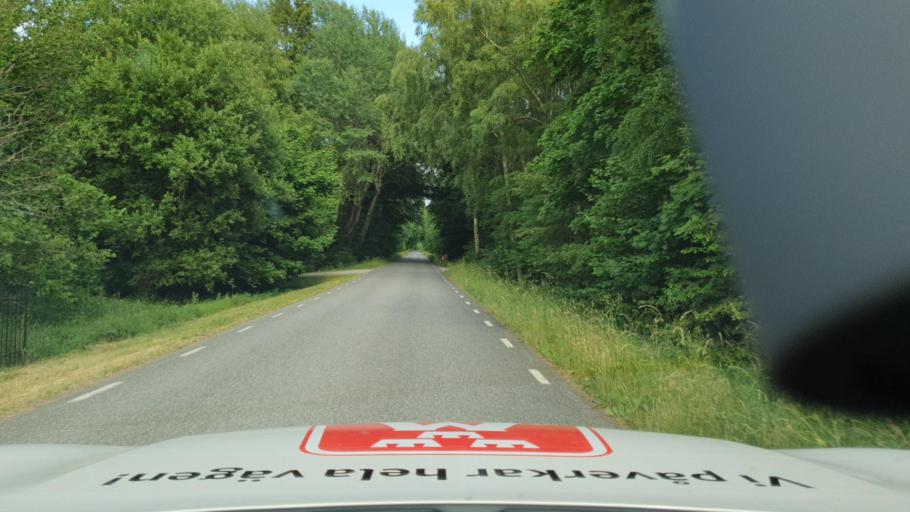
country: SE
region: Skane
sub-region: Simrishamns Kommun
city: Kivik
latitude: 55.6866
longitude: 14.1058
